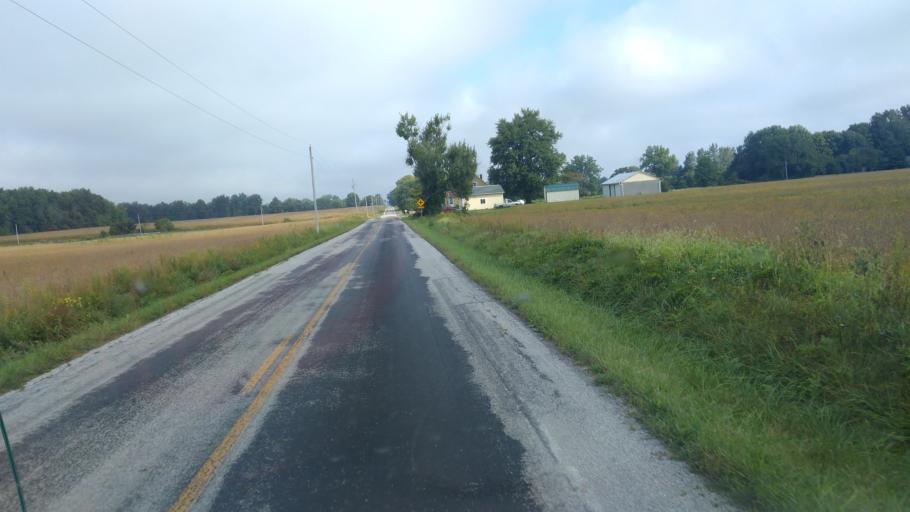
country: US
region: Ohio
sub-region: Morrow County
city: Cardington
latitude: 40.5478
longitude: -82.9766
